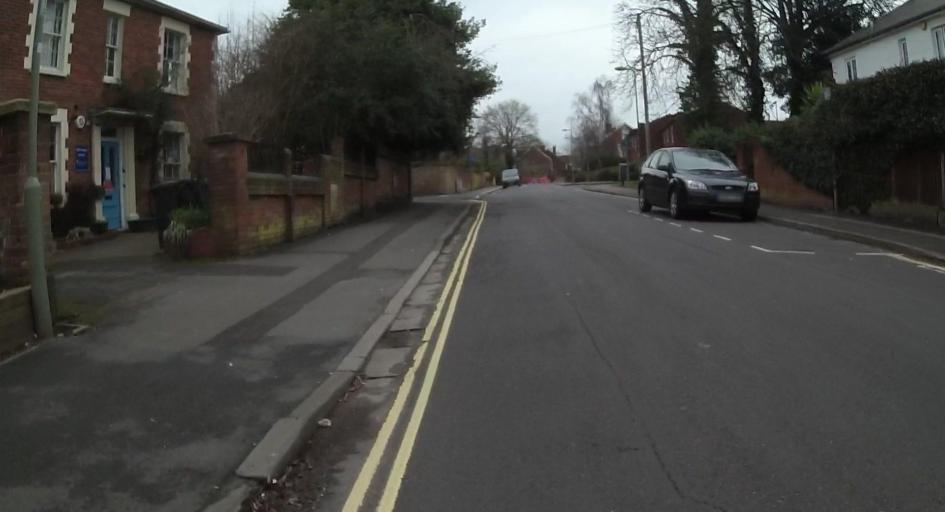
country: GB
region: England
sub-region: Hampshire
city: Basingstoke
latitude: 51.2706
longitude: -1.0893
